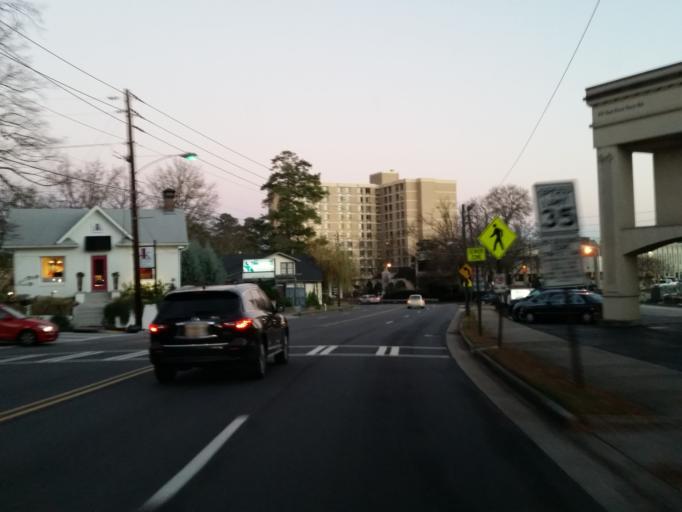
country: US
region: Georgia
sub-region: DeKalb County
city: North Atlanta
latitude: 33.8385
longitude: -84.3744
